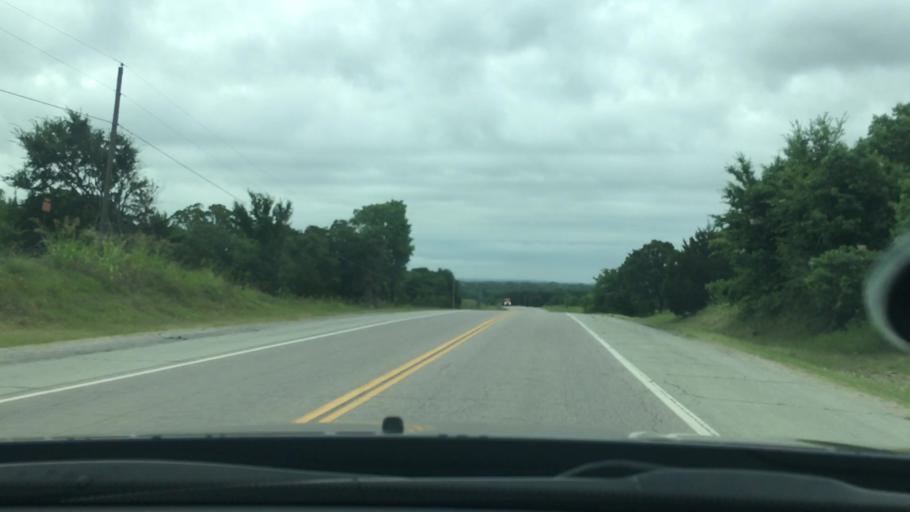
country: US
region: Oklahoma
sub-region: Coal County
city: Coalgate
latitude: 34.5557
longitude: -96.2404
